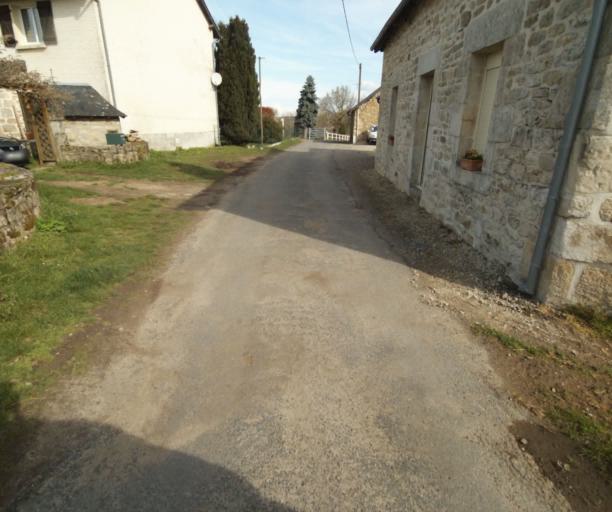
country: FR
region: Limousin
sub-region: Departement de la Correze
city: Correze
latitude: 45.3410
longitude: 1.8320
